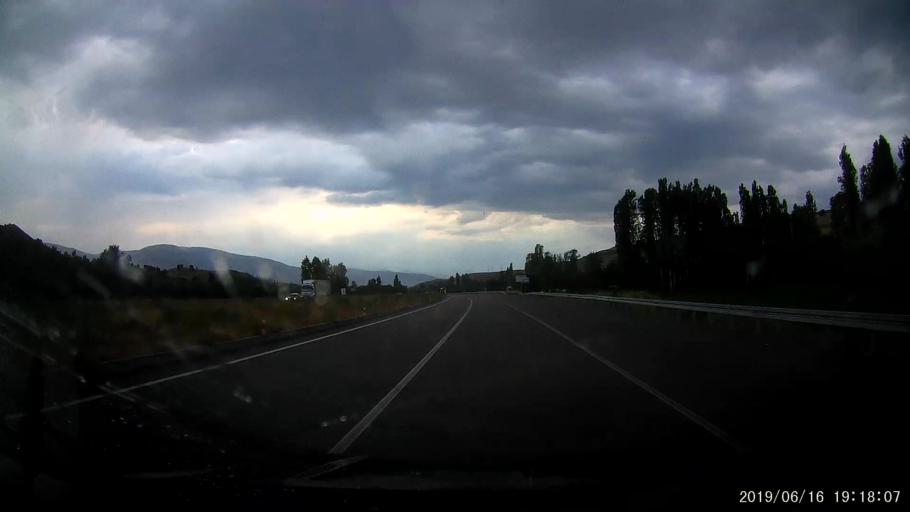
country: TR
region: Sivas
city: Akincilar
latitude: 40.0947
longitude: 38.4668
